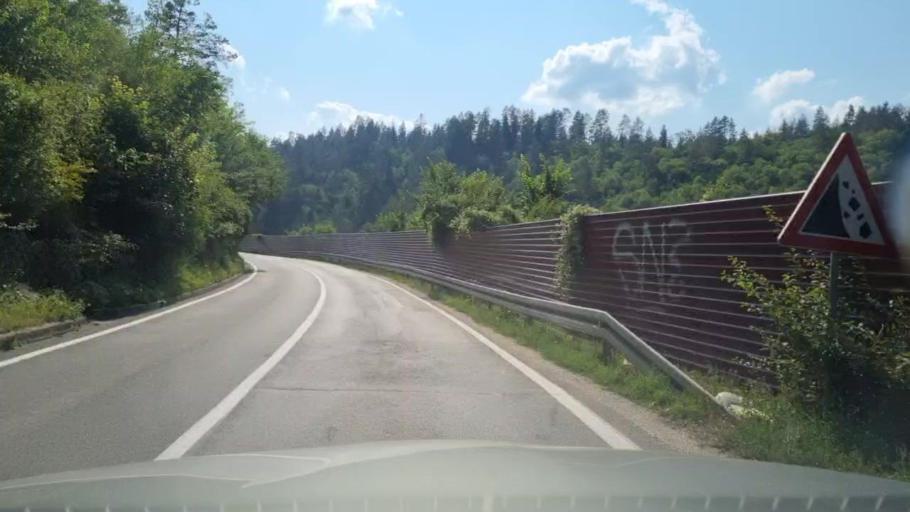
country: BA
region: Federation of Bosnia and Herzegovina
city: Olovo
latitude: 44.1229
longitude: 18.5711
